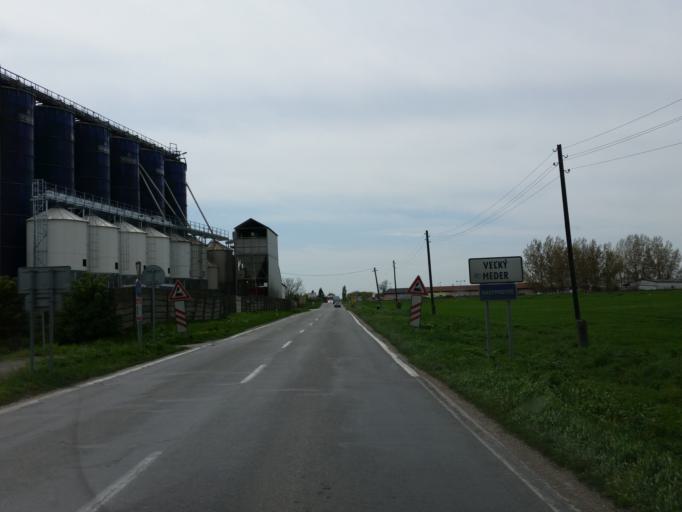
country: SK
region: Trnavsky
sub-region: Okres Dunajska Streda
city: Velky Meder
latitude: 47.8654
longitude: 17.7830
